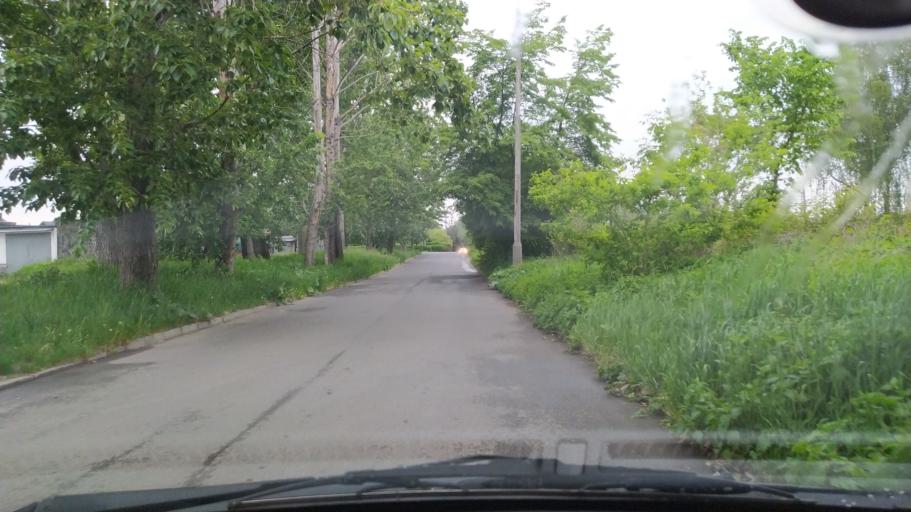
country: PL
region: Silesian Voivodeship
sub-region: Powiat gliwicki
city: Przyszowice
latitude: 50.2956
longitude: 18.7288
